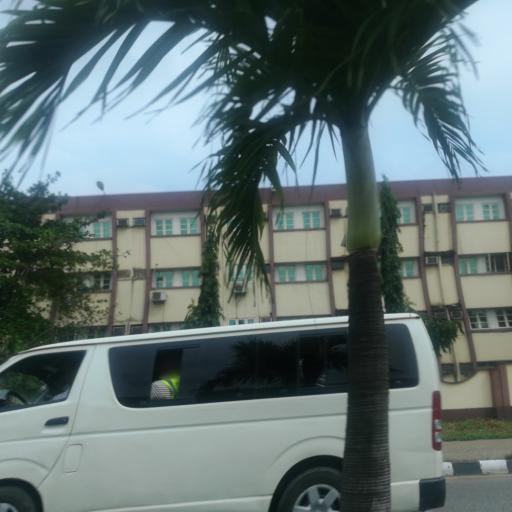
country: NG
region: Lagos
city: Ikeja
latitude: 6.6133
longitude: 3.3607
